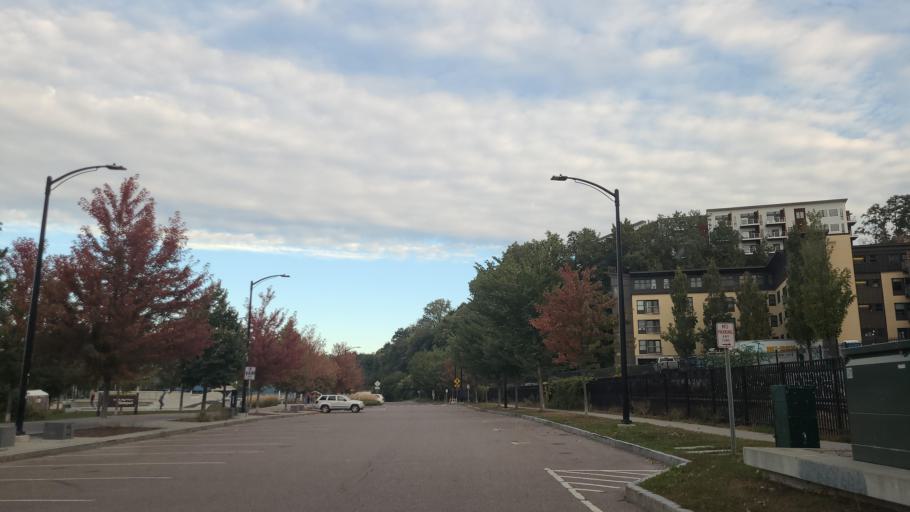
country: US
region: Vermont
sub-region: Chittenden County
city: Burlington
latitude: 44.4821
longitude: -73.2228
